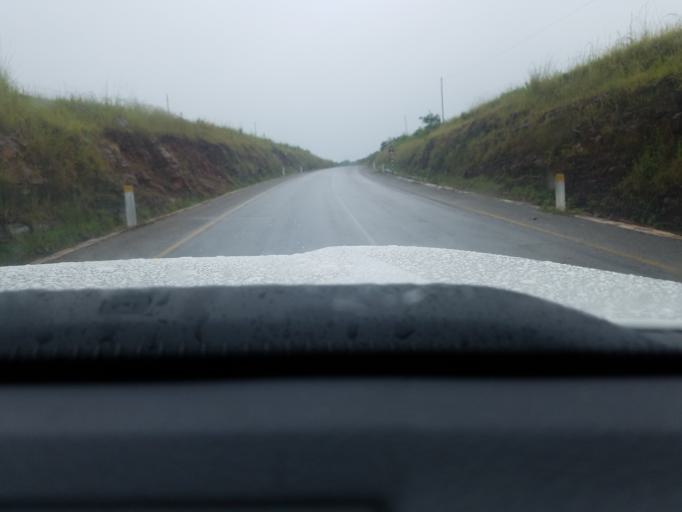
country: TZ
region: Kigoma
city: Mwandiga
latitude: -4.6624
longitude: 29.7238
